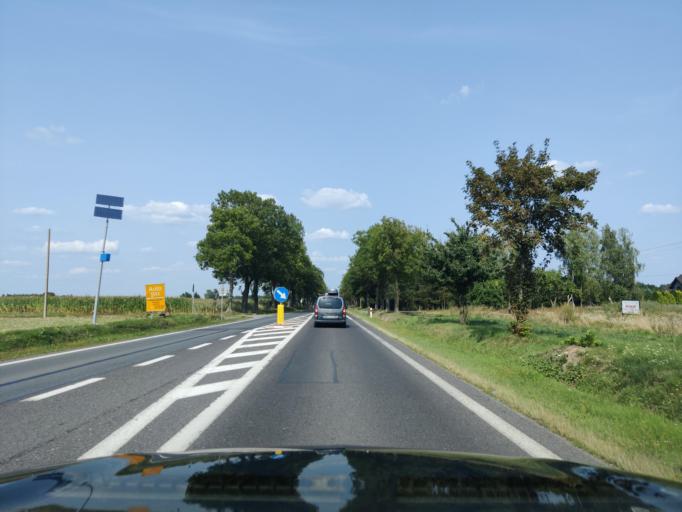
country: PL
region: Masovian Voivodeship
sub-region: Powiat pultuski
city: Pultusk
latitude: 52.7712
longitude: 21.1185
